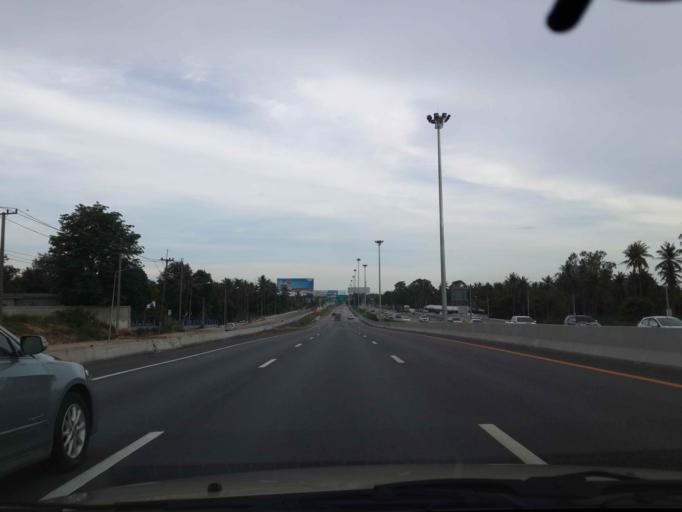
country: TH
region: Chon Buri
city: Bang Lamung
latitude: 12.9798
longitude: 100.9854
